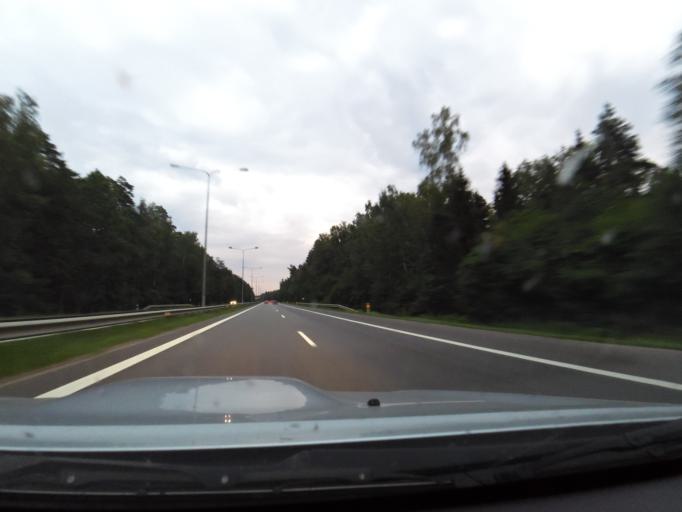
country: LT
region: Kauno apskritis
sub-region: Kauno rajonas
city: Karmelava
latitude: 54.8929
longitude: 24.1580
